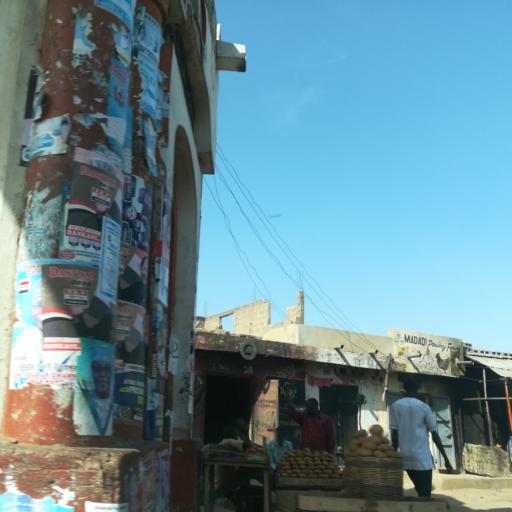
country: NG
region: Kano
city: Kano
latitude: 12.0150
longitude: 8.5181
